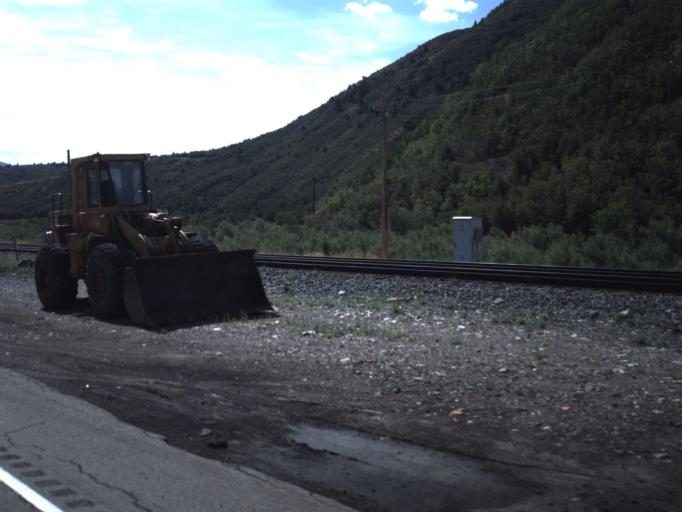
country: US
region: Utah
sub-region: Utah County
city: Mapleton
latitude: 40.0368
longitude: -111.5300
